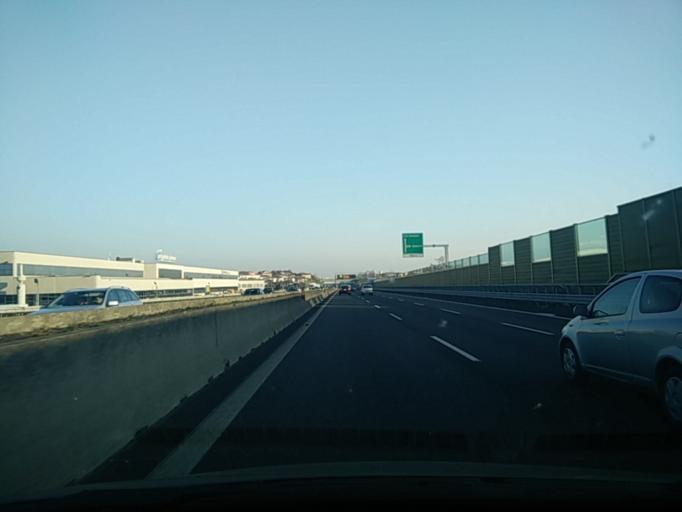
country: IT
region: Lombardy
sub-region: Provincia di Bergamo
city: Grassobbio
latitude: 45.6576
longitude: 9.7370
